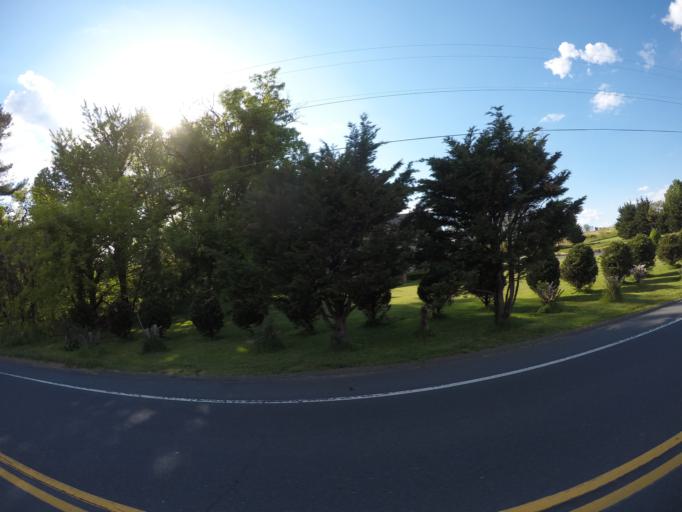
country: US
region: Maryland
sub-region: Montgomery County
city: Damascus
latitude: 39.3284
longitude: -77.1893
